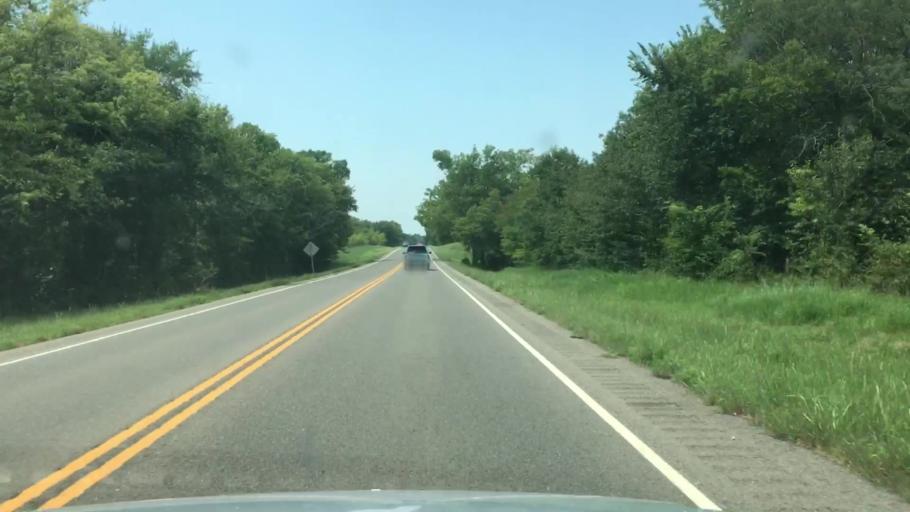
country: US
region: Oklahoma
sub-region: Wagoner County
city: Wagoner
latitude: 35.9394
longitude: -95.3045
